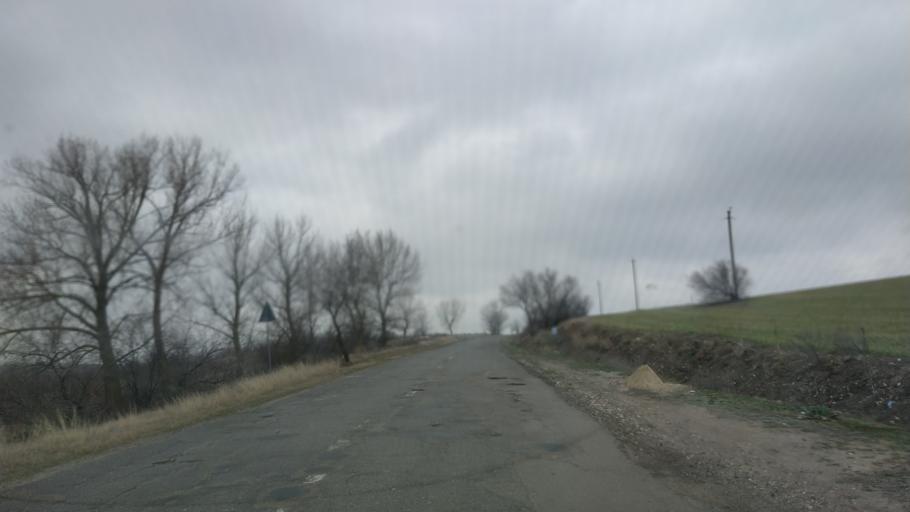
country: MD
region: Gagauzia
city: Bugeac
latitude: 46.3543
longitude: 28.7935
